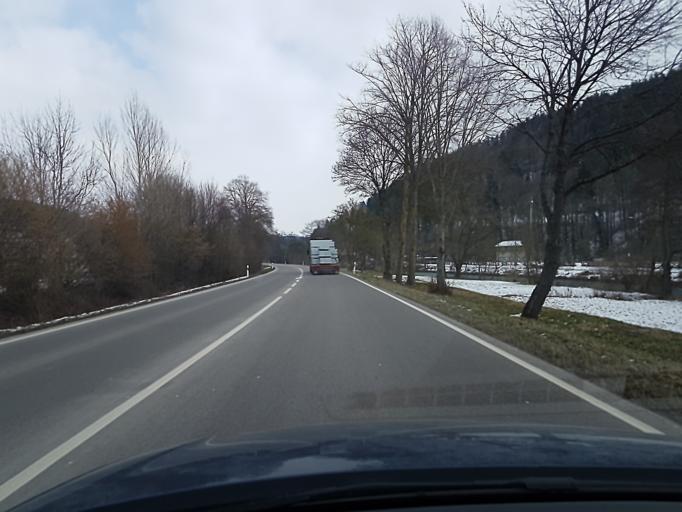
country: DE
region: Baden-Wuerttemberg
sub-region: Karlsruhe Region
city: Horb am Neckar
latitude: 48.4380
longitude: 8.6772
